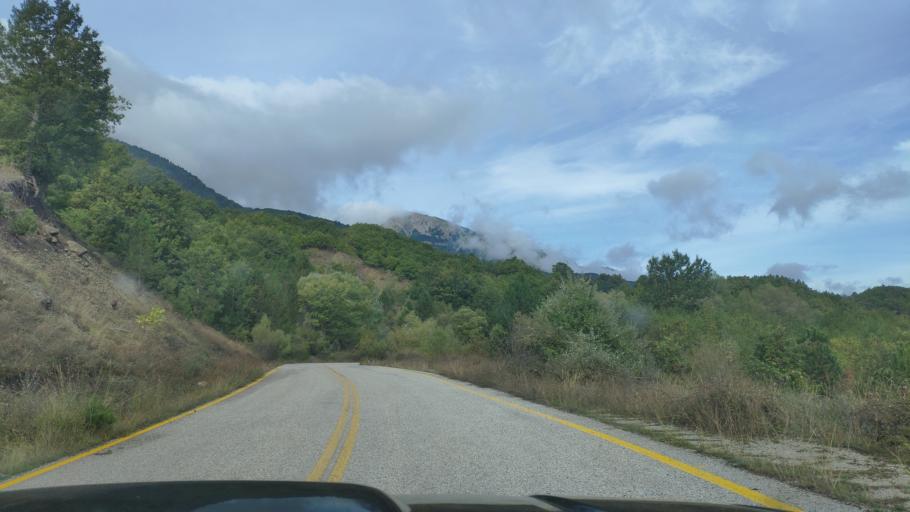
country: GR
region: West Macedonia
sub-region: Nomos Kastorias
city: Nestorio
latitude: 40.2451
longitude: 20.9890
